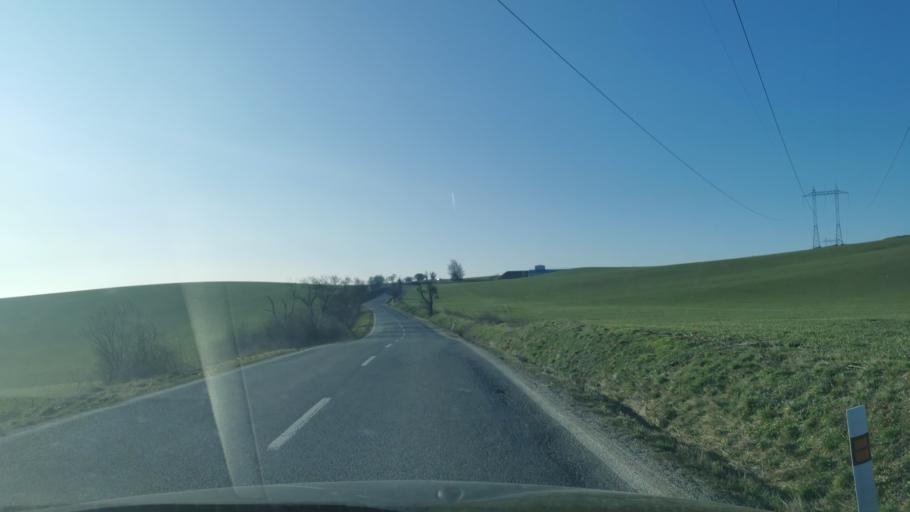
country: SK
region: Trnavsky
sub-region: Okres Senica
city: Senica
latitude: 48.7354
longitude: 17.3836
